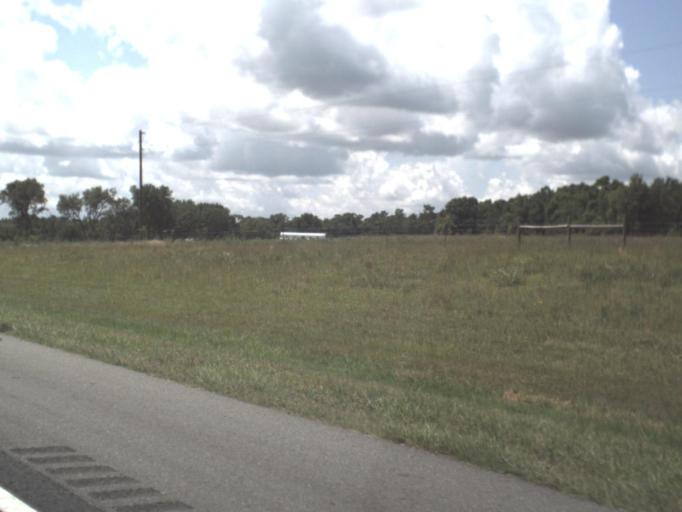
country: US
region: Florida
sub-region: Suwannee County
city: Wellborn
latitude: 30.3289
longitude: -82.8192
